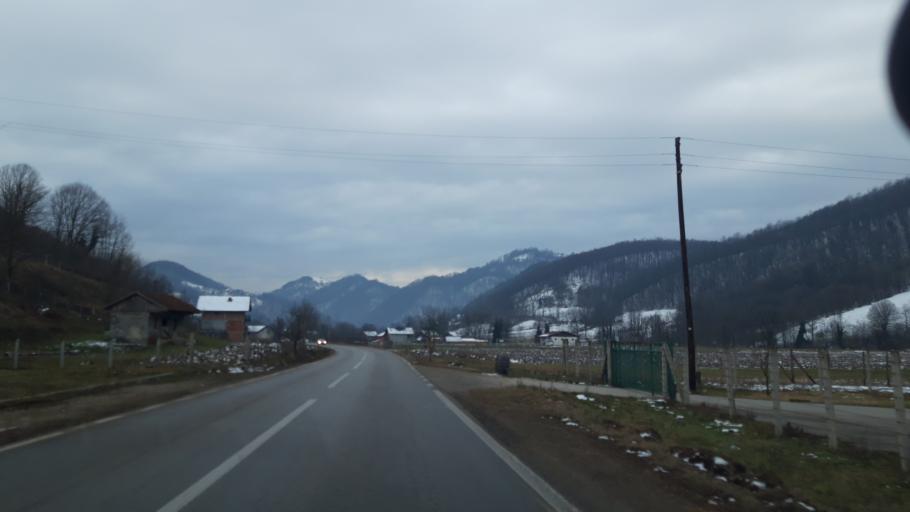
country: BA
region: Republika Srpska
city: Milici
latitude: 44.2219
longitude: 19.1000
